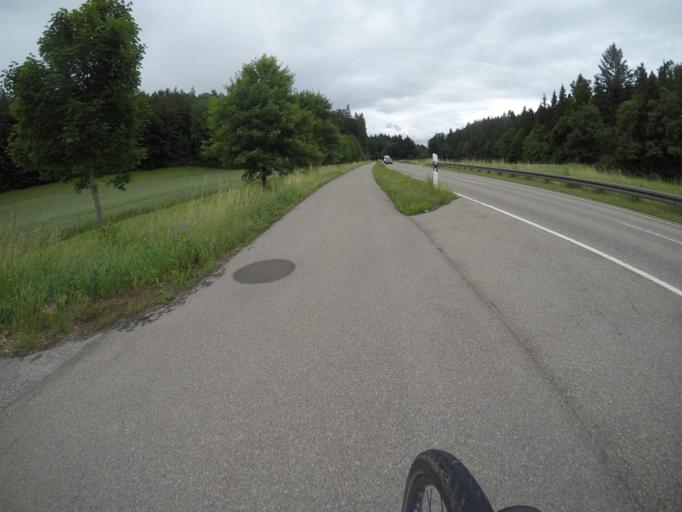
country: DE
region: Baden-Wuerttemberg
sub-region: Regierungsbezirk Stuttgart
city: Aidlingen
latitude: 48.6606
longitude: 8.8792
